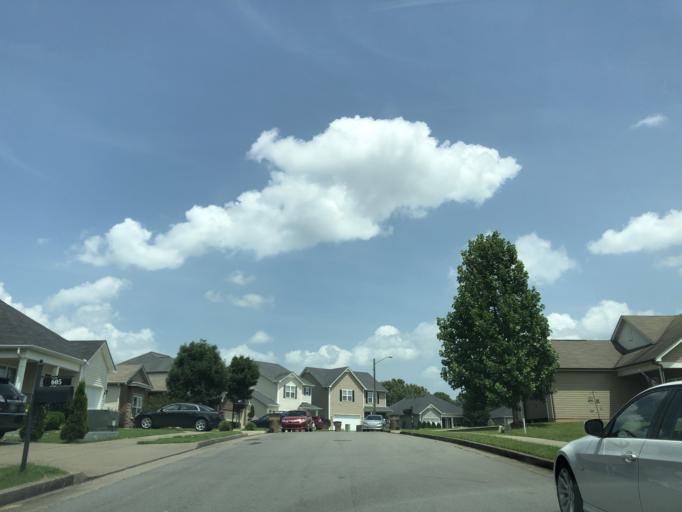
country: US
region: Tennessee
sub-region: Williamson County
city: Brentwood Estates
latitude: 36.0569
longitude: -86.6927
